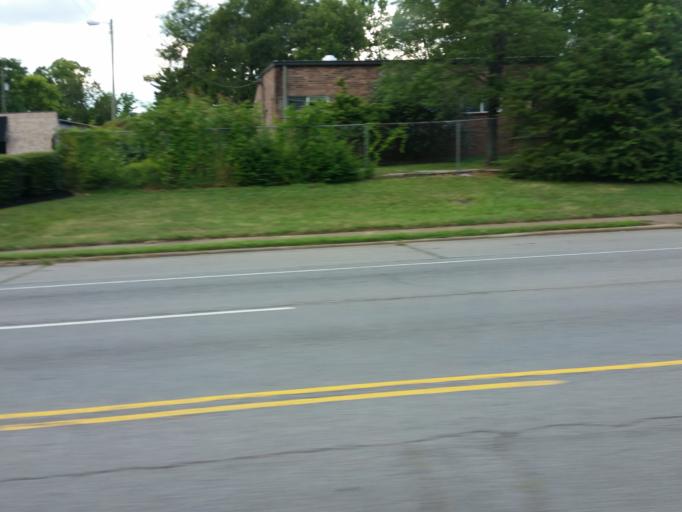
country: US
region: Tennessee
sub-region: Davidson County
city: Nashville
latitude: 36.2233
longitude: -86.7257
